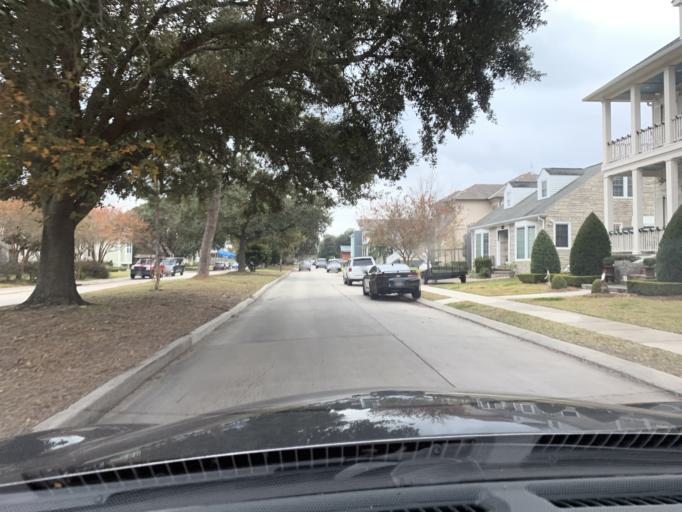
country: US
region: Louisiana
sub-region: Jefferson Parish
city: Metairie
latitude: 30.0063
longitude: -90.1025
